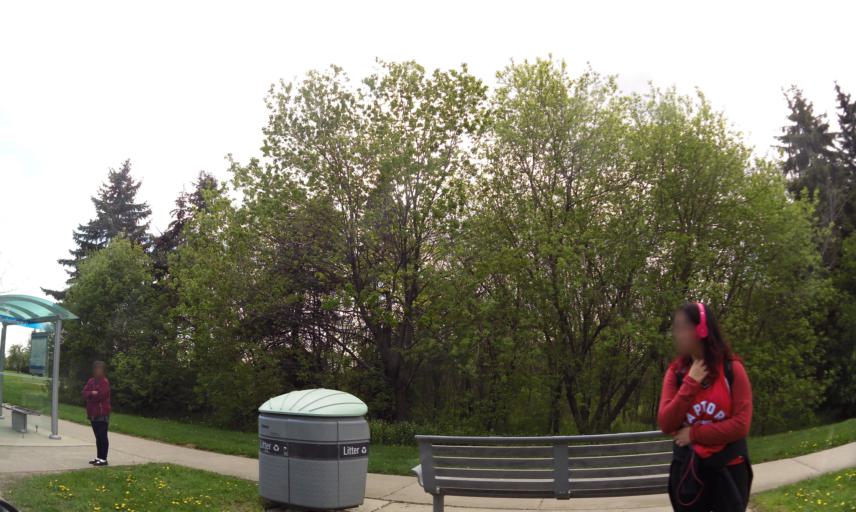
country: CA
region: Ontario
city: Etobicoke
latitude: 43.6472
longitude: -79.5679
